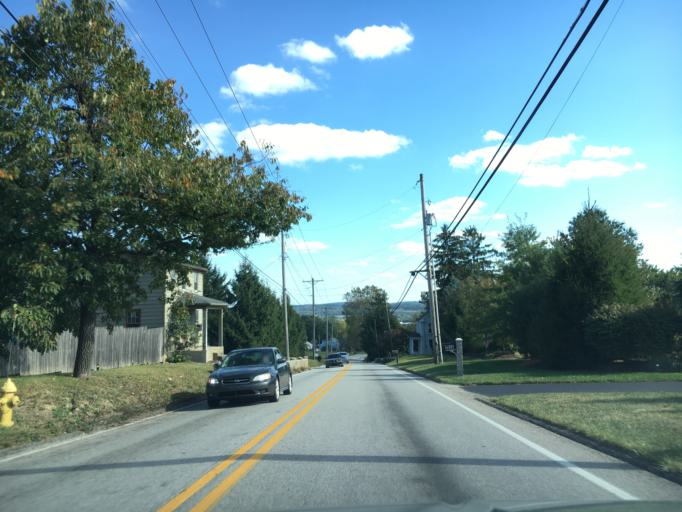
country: US
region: Pennsylvania
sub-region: York County
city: East York
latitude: 39.9998
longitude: -76.6799
